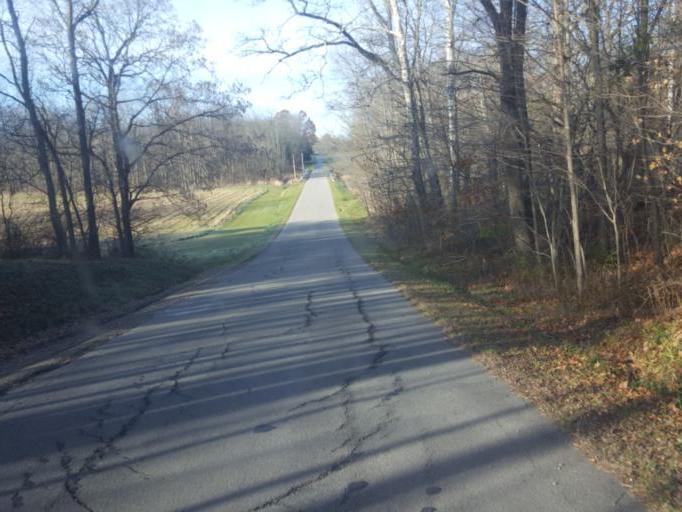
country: US
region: Ohio
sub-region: Crawford County
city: Bucyrus
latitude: 40.7549
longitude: -82.8942
